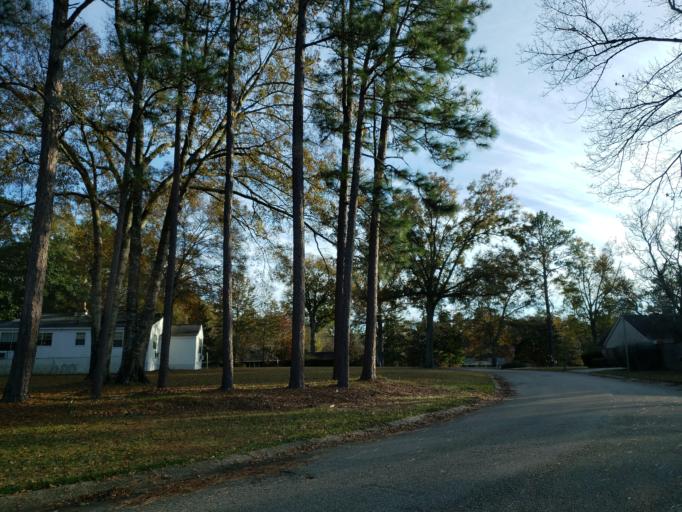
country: US
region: Mississippi
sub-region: Lamar County
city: West Hattiesburg
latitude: 31.2968
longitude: -89.3344
